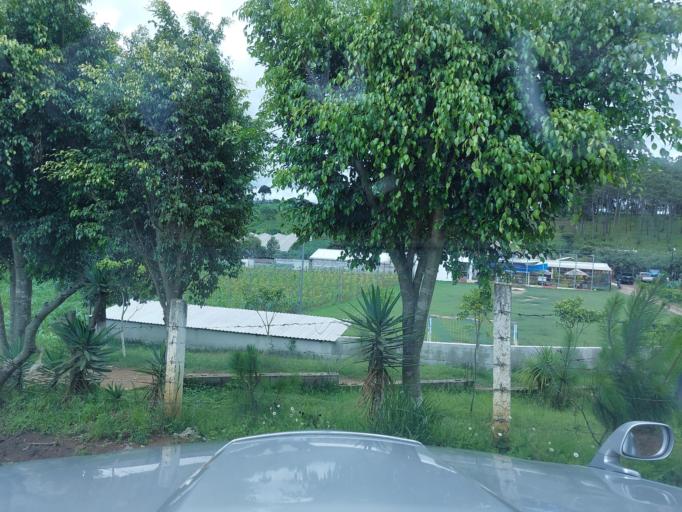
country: GT
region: Chimaltenango
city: San Andres Itzapa
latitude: 14.6394
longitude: -90.8302
